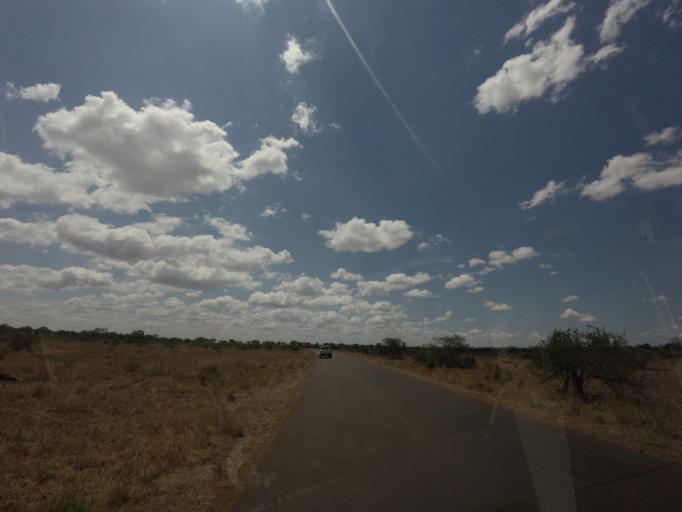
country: ZA
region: Limpopo
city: Thulamahashi
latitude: -24.3967
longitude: 31.7862
